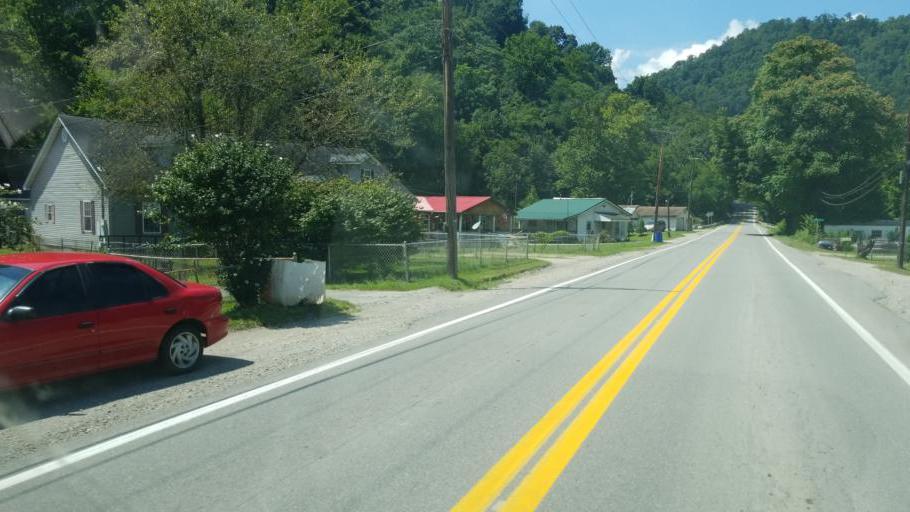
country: US
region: West Virginia
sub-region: Kanawha County
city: Chesapeake
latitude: 38.1806
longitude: -81.4672
